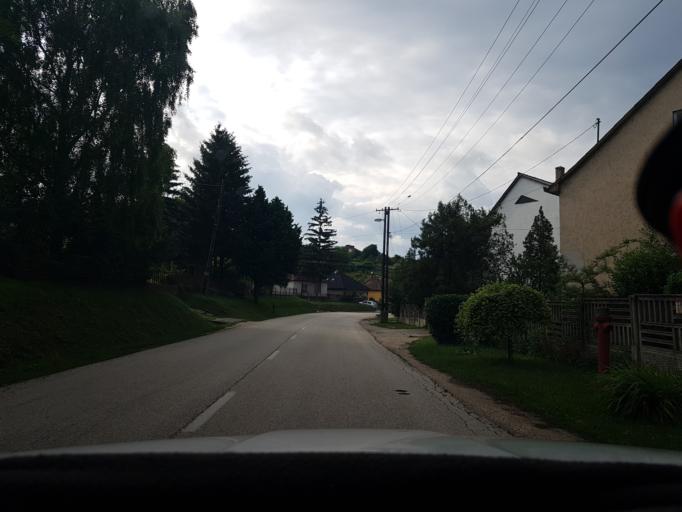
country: HU
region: Komarom-Esztergom
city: Nyergesujfalu
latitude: 47.7190
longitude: 18.5624
